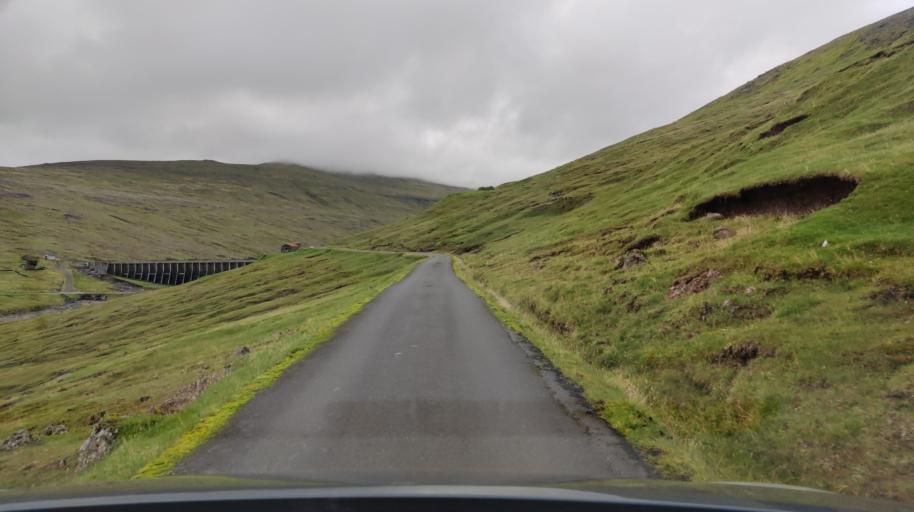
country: FO
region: Streymoy
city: Vestmanna
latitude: 62.1739
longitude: -7.1484
